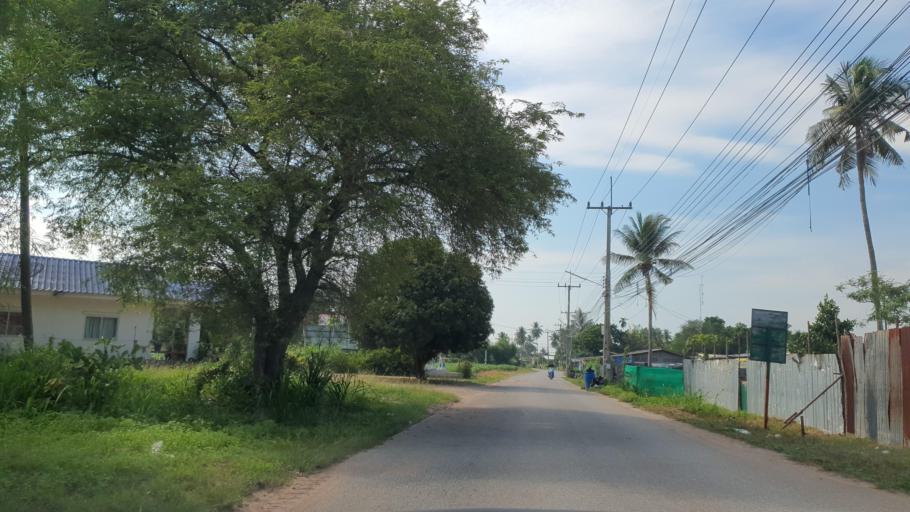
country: TH
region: Rayong
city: Ban Chang
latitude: 12.7880
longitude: 100.9434
